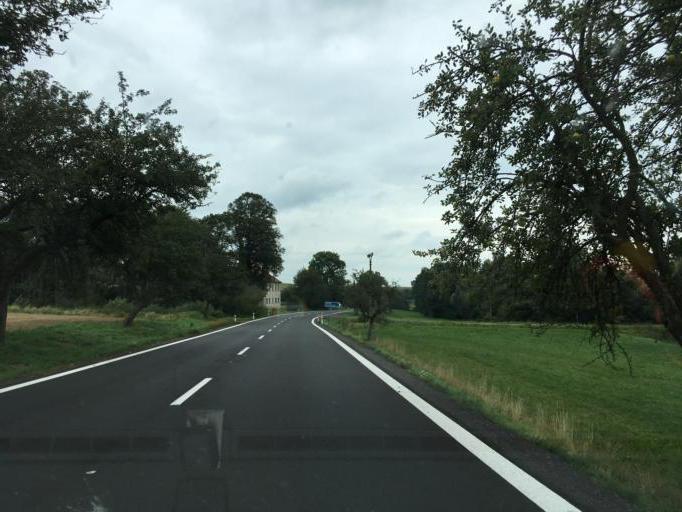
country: CZ
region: Central Bohemia
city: Cechtice
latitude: 49.5886
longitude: 15.0771
